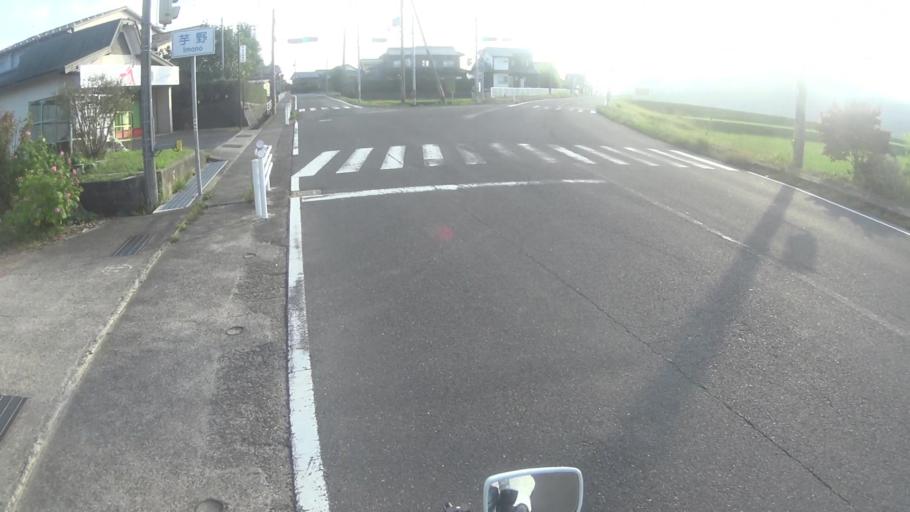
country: JP
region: Kyoto
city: Miyazu
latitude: 35.6503
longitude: 135.0918
